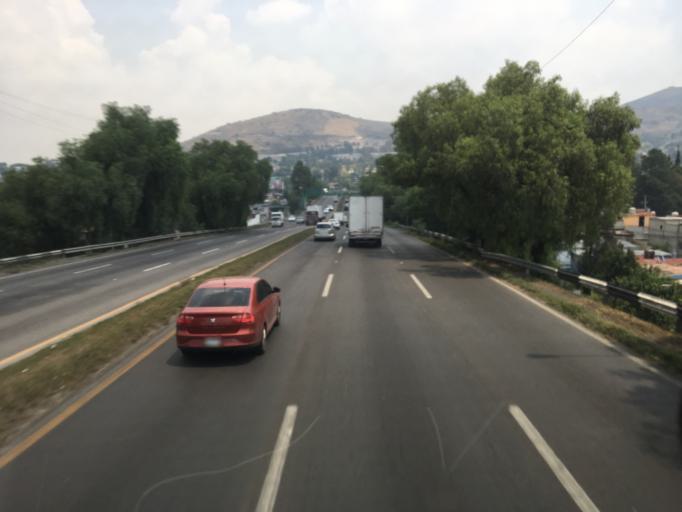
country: MX
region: Mexico
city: Tlalnepantla
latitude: 19.5549
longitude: -99.1850
